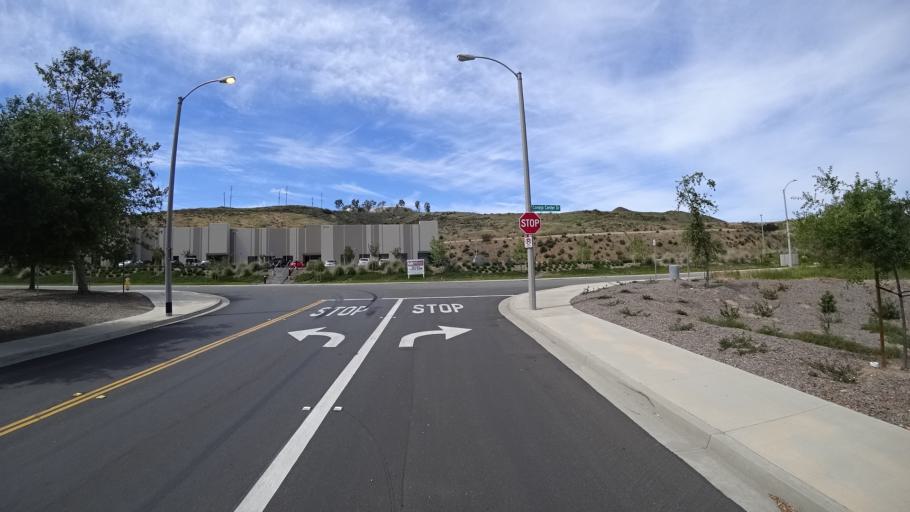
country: US
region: California
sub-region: Ventura County
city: Casa Conejo
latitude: 34.2001
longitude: -118.9339
